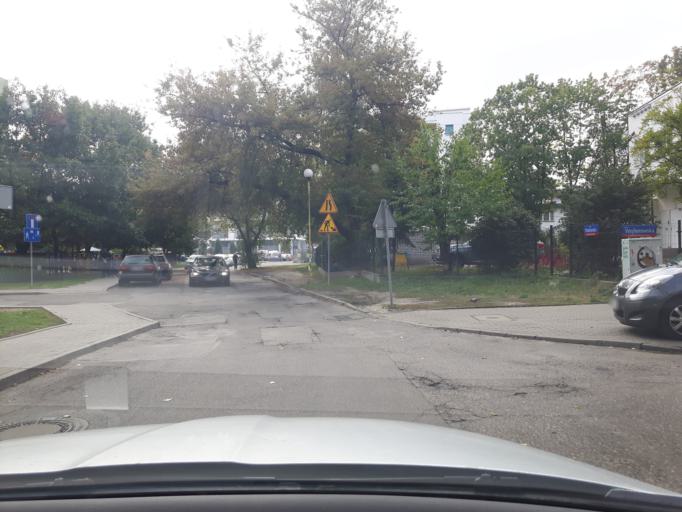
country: PL
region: Masovian Voivodeship
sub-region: Warszawa
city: Targowek
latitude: 52.2715
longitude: 21.0489
